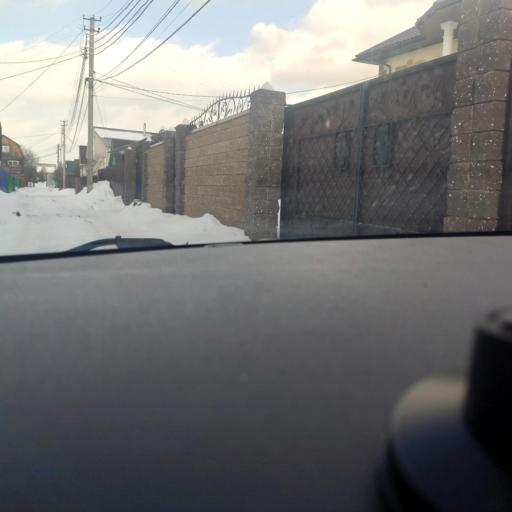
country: RU
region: Bashkortostan
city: Ufa
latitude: 54.6877
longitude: 55.9035
